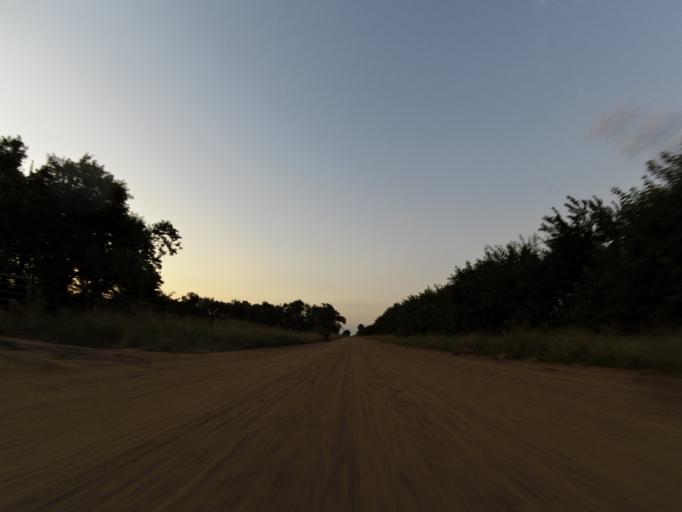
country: US
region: Kansas
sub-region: Reno County
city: South Hutchinson
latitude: 37.9662
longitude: -98.0319
